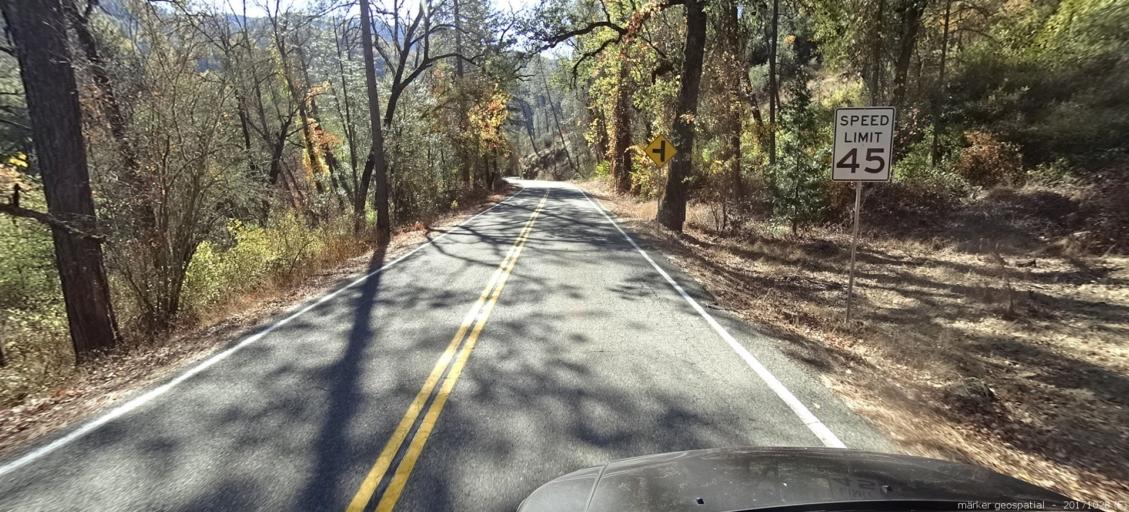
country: US
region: California
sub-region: Trinity County
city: Lewiston
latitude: 40.7541
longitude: -122.6172
